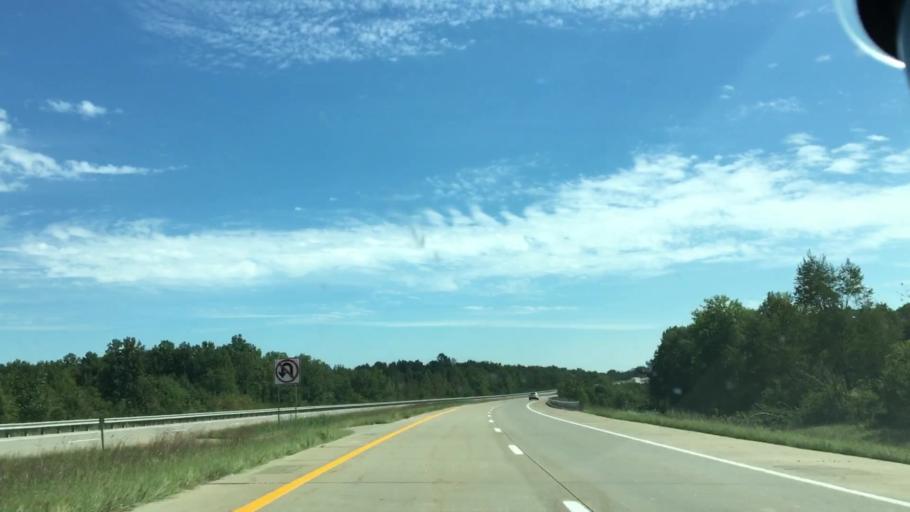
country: US
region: Kentucky
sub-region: Daviess County
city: Owensboro
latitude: 37.7622
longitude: -87.3051
